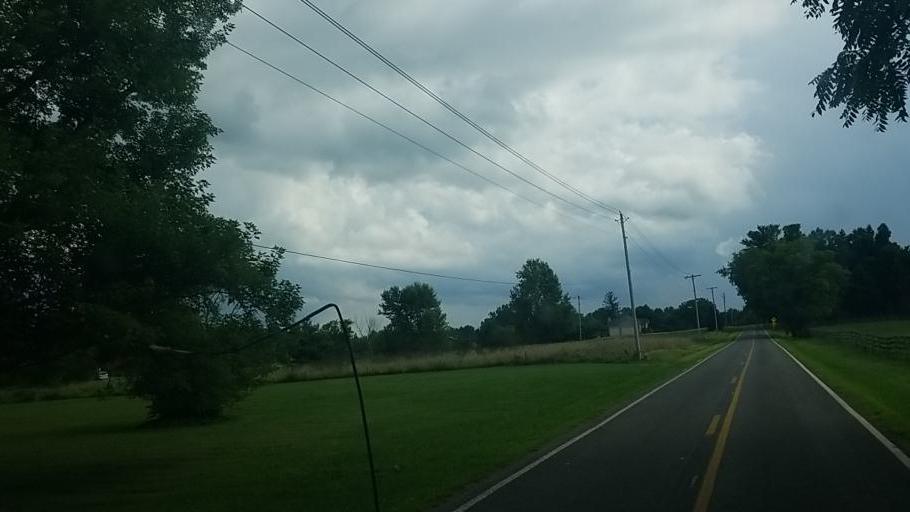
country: US
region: Ohio
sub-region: Wayne County
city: Creston
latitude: 40.9989
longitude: -81.9102
